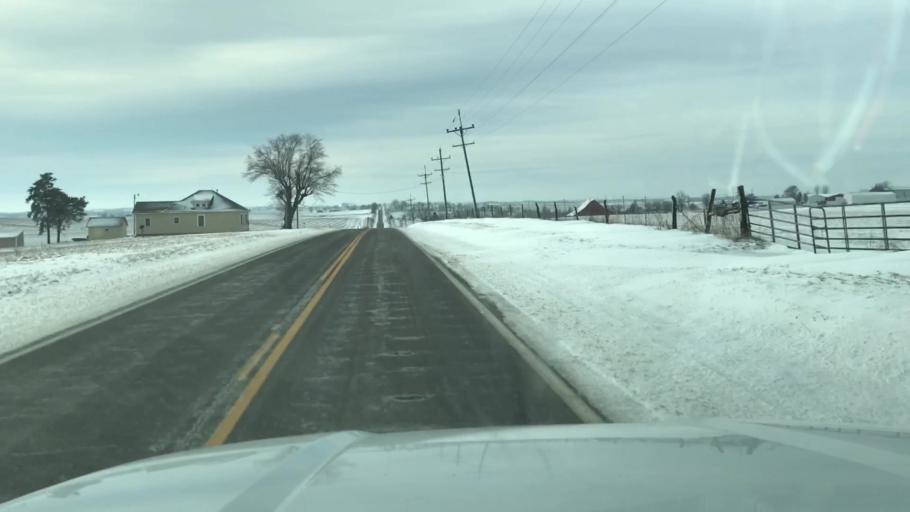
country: US
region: Missouri
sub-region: Holt County
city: Oregon
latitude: 40.0843
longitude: -95.1355
